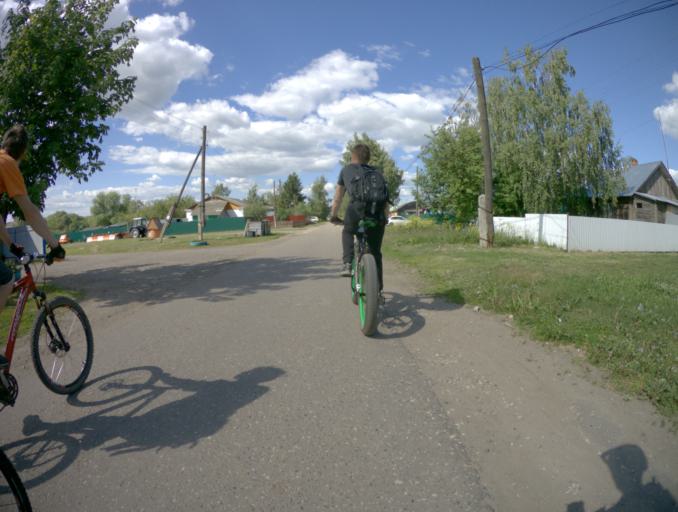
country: RU
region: Vladimir
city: Suzdal'
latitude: 56.3408
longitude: 40.3357
